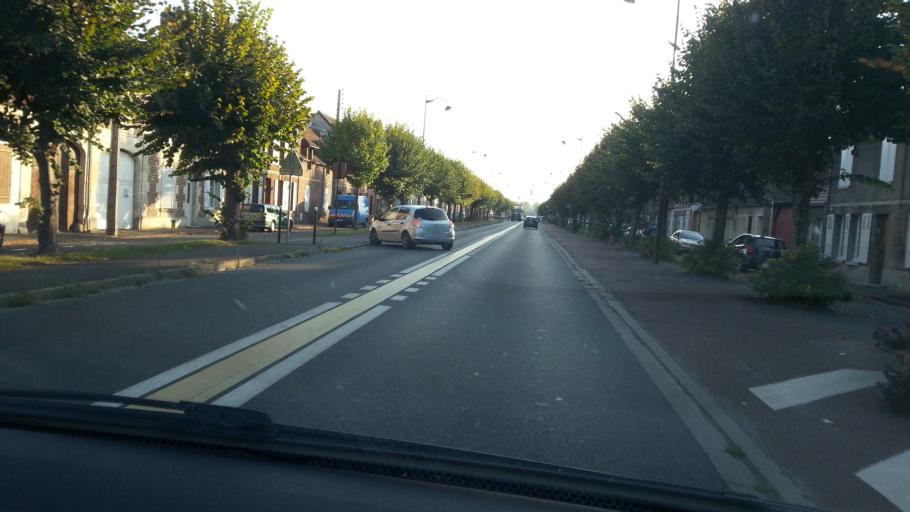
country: FR
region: Picardie
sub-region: Departement de l'Oise
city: Estrees-Saint-Denis
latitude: 49.4291
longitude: 2.6394
